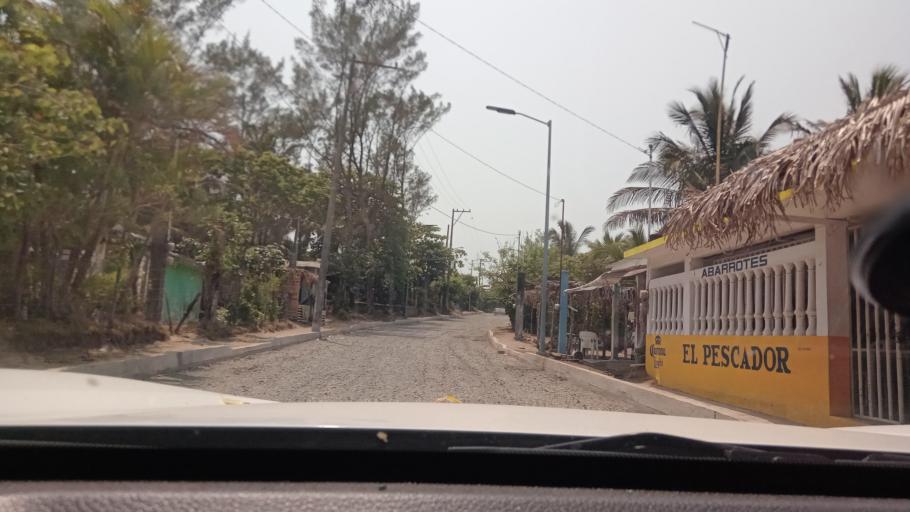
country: MX
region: Veracruz
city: Catemaco
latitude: 18.5564
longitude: -94.9913
